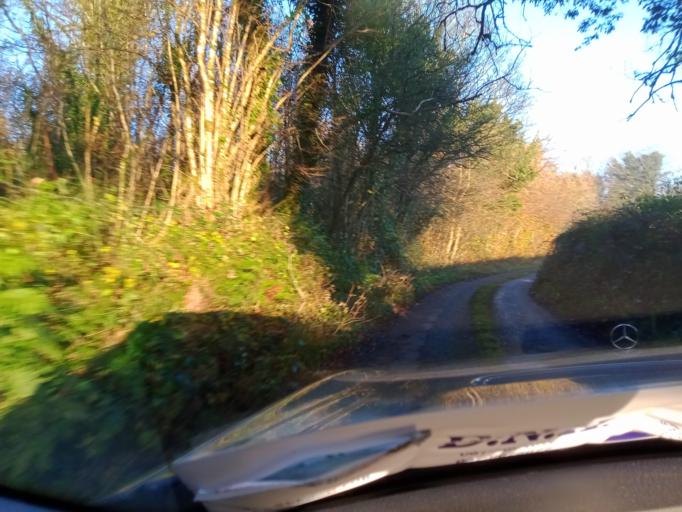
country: IE
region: Leinster
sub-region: Kilkenny
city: Callan
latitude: 52.5301
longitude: -7.4476
